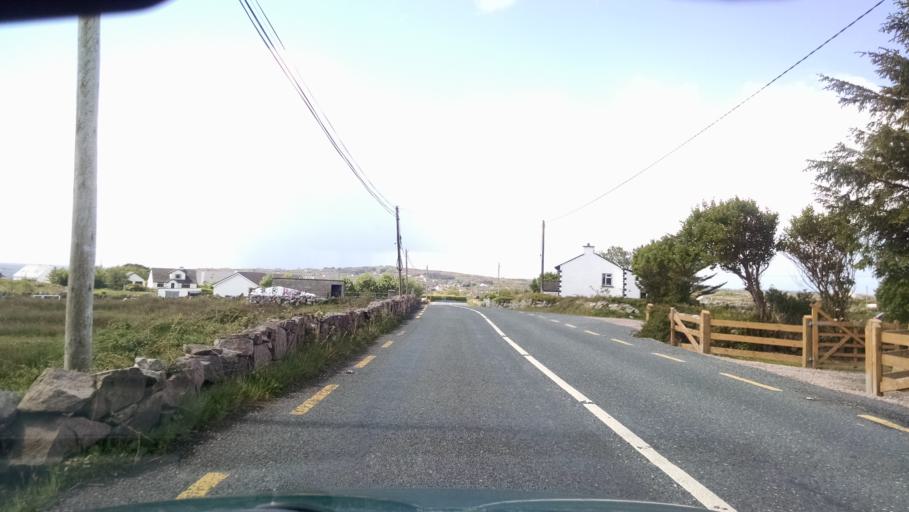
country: IE
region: Connaught
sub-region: County Galway
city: Oughterard
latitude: 53.2843
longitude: -9.5678
